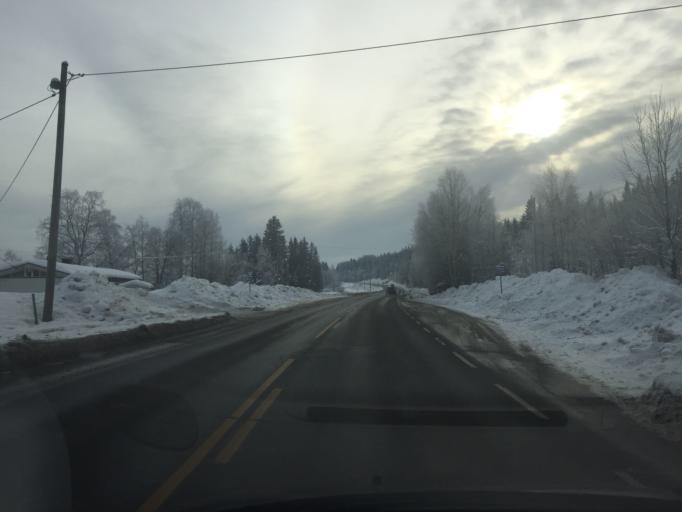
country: NO
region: Hedmark
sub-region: Trysil
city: Innbygda
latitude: 61.3258
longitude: 12.2371
